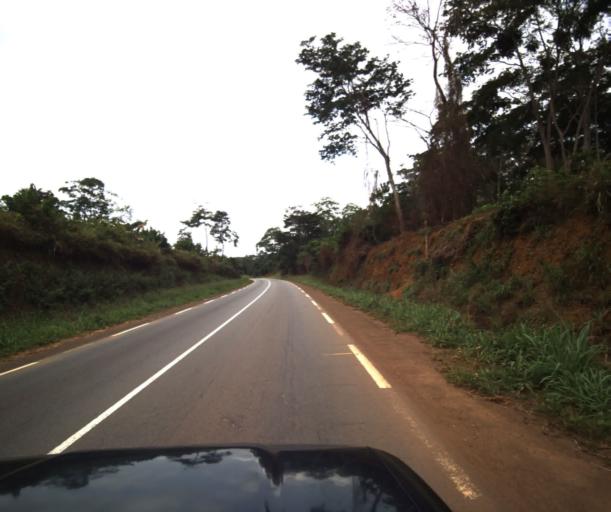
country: CM
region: Centre
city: Eseka
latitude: 3.8699
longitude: 10.9157
